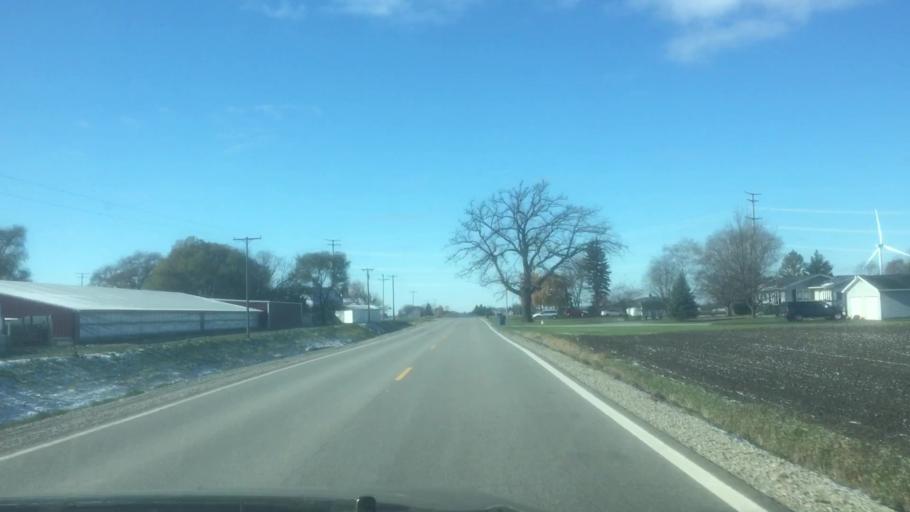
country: US
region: Michigan
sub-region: Tuscola County
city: Reese
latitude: 43.5230
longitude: -83.6199
